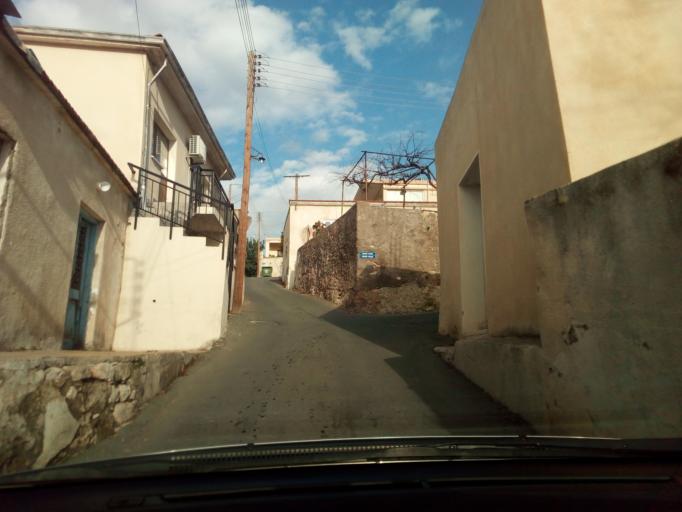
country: CY
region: Pafos
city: Mesogi
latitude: 34.8145
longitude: 32.4575
